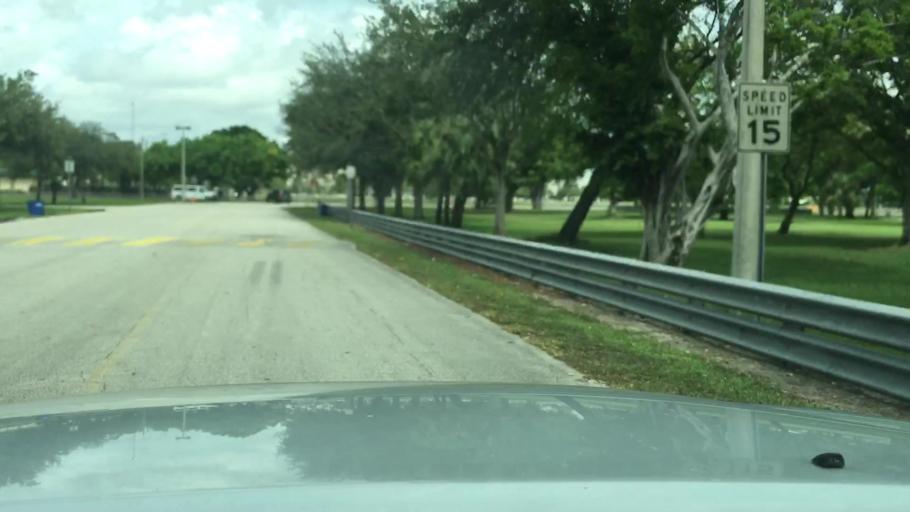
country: US
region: Florida
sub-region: Miami-Dade County
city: University Park
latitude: 25.7477
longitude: -80.3759
